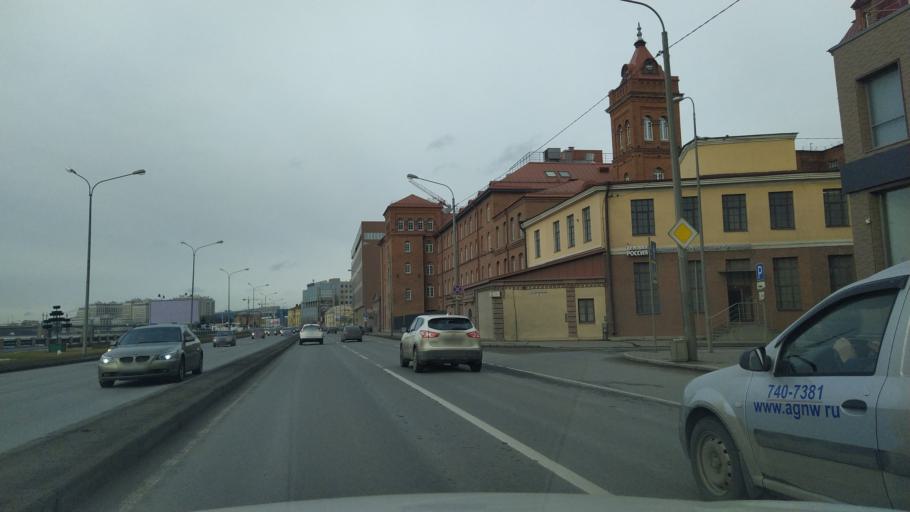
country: RU
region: Leningrad
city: Sampsonievskiy
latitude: 59.9737
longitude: 30.3332
